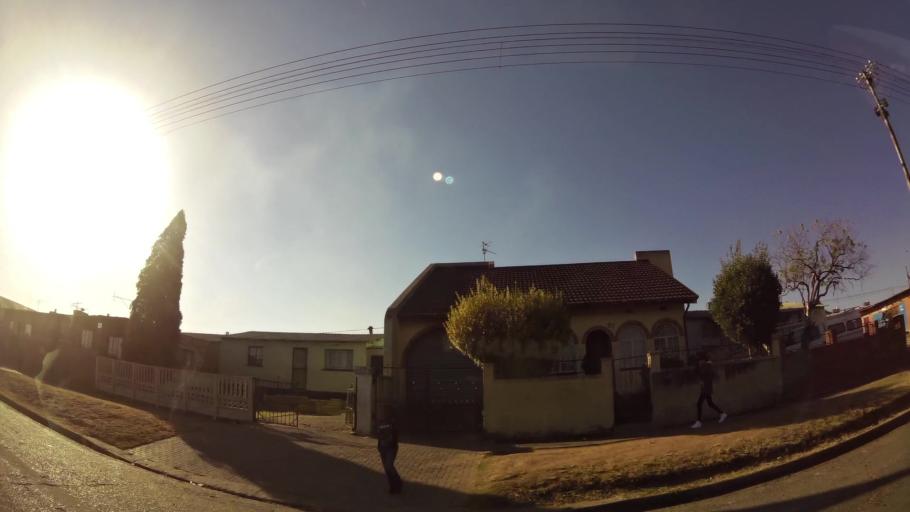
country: ZA
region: Gauteng
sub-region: City of Johannesburg Metropolitan Municipality
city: Johannesburg
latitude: -26.2169
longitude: 27.9788
